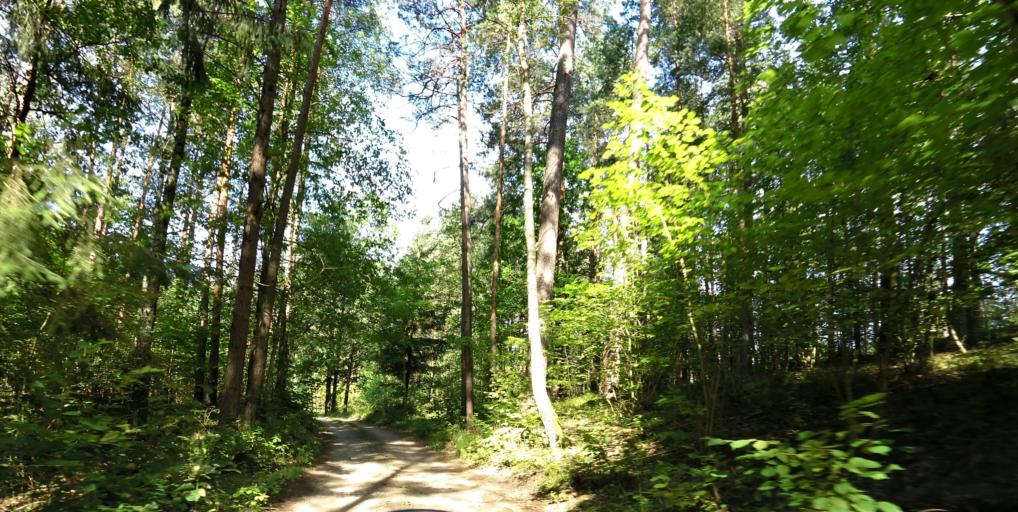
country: LT
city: Grigiskes
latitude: 54.7412
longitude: 25.0282
